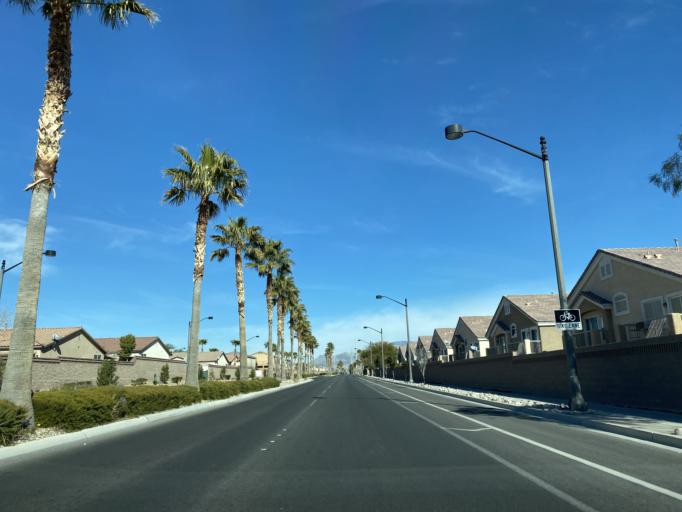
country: US
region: Nevada
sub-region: Clark County
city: Summerlin South
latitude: 36.2885
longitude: -115.2968
